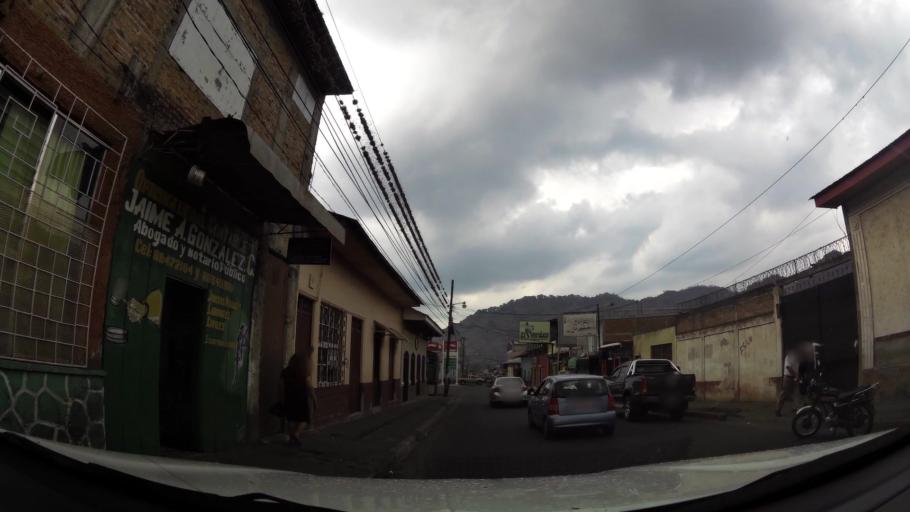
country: NI
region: Jinotega
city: Jinotega
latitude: 13.0925
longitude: -86.0018
